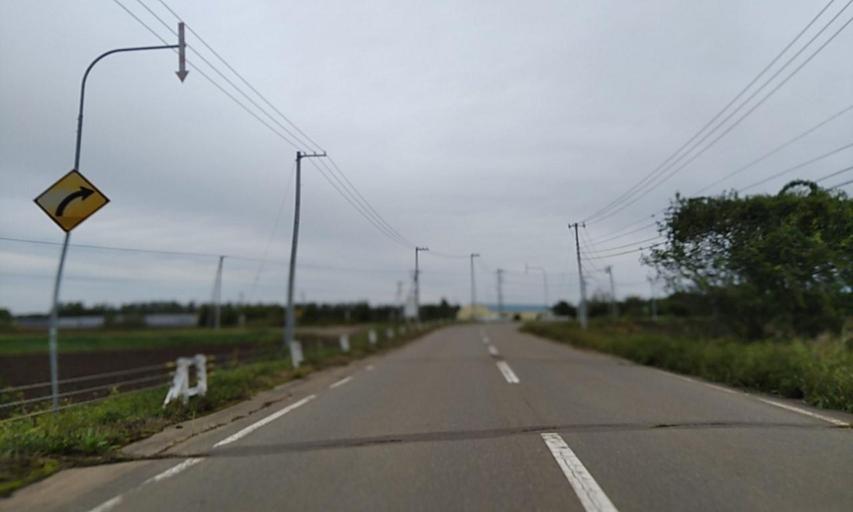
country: JP
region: Hokkaido
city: Obihiro
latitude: 42.6253
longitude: 143.2621
